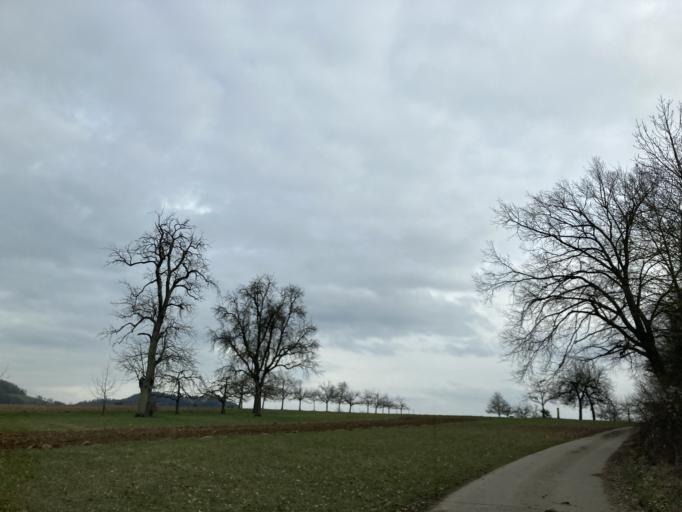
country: DE
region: Baden-Wuerttemberg
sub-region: Tuebingen Region
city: Rottenburg
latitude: 48.4563
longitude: 8.9063
